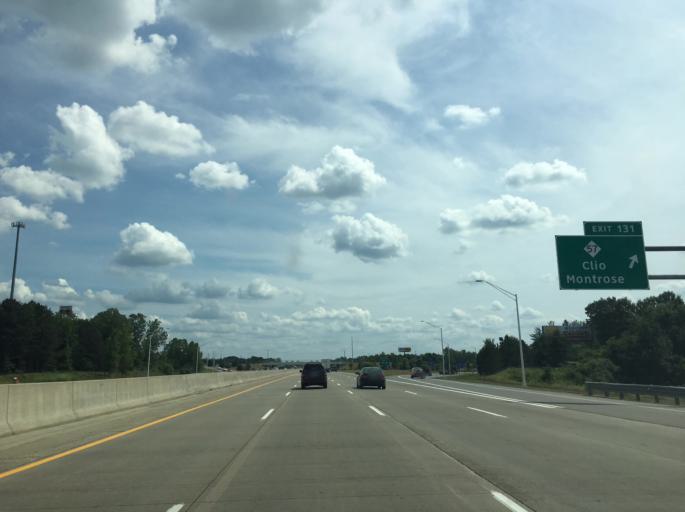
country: US
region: Michigan
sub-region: Genesee County
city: Clio
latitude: 43.1827
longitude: -83.7689
